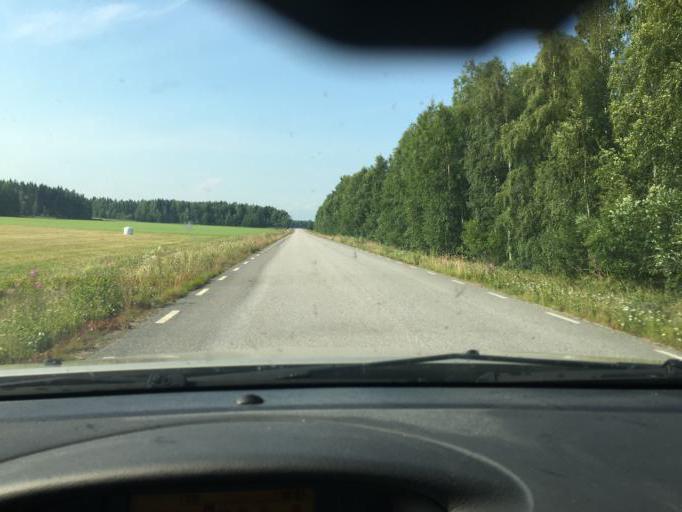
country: SE
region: Norrbotten
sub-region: Kalix Kommun
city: Toere
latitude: 65.8747
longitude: 22.6718
